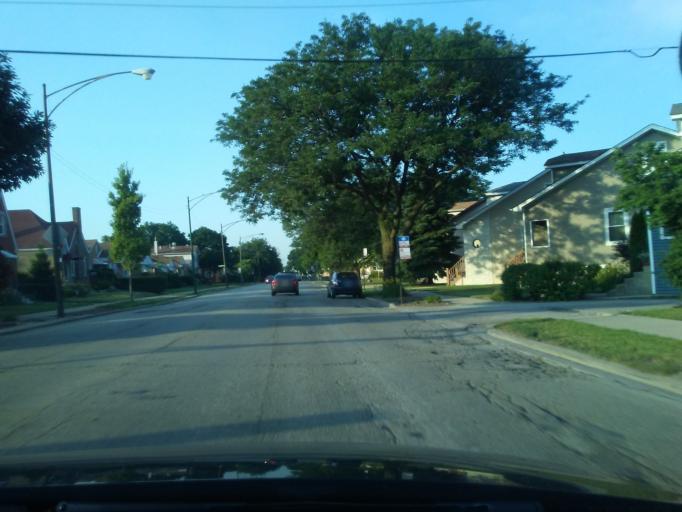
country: US
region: Illinois
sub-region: Cook County
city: Harwood Heights
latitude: 41.9897
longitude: -87.7877
